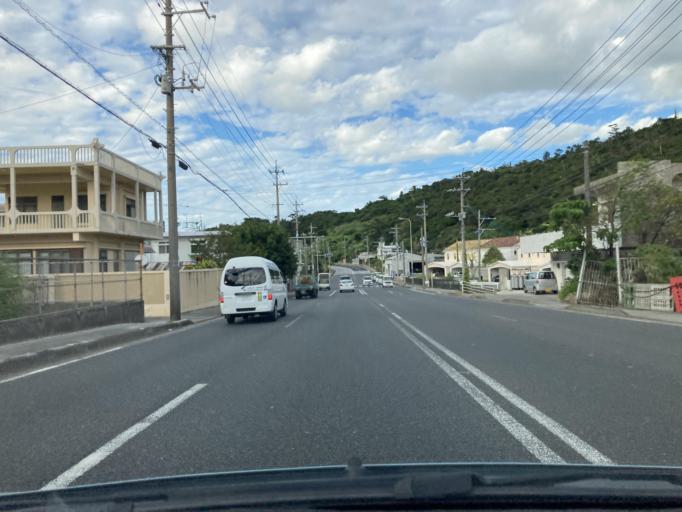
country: JP
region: Okinawa
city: Ishikawa
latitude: 26.3953
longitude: 127.8326
